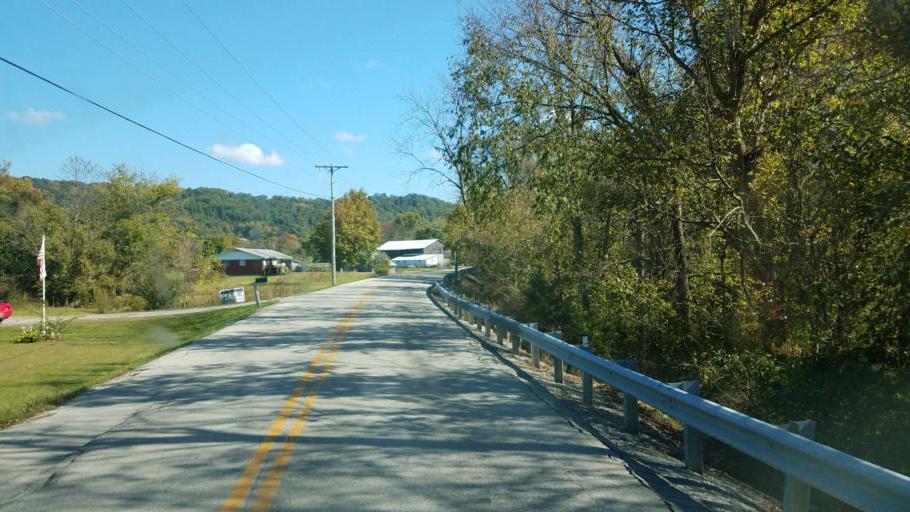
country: US
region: Kentucky
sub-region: Fleming County
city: Flemingsburg
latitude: 38.4738
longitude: -83.5871
